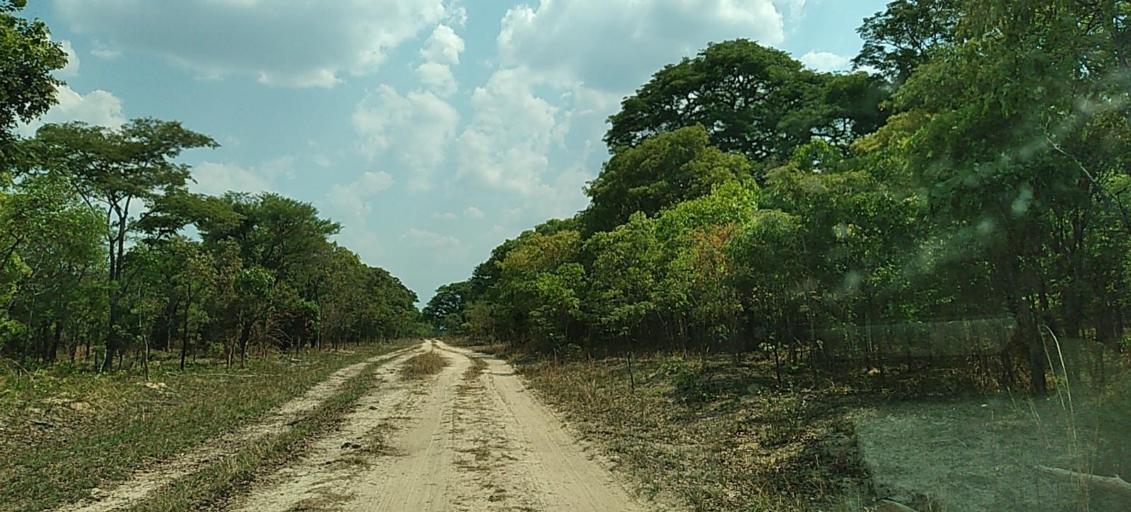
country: ZM
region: Copperbelt
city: Mpongwe
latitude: -13.8449
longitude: 27.9340
